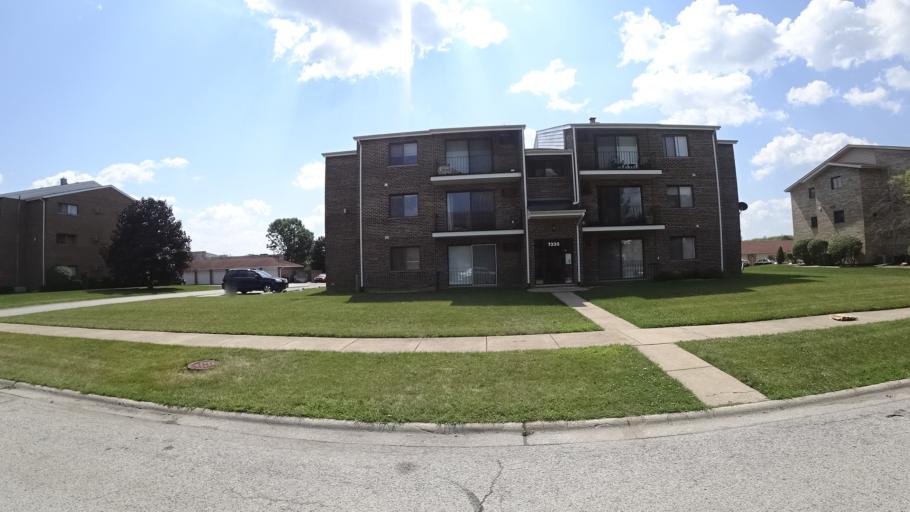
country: US
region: Illinois
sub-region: Cook County
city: Tinley Park
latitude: 41.6047
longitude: -87.7984
